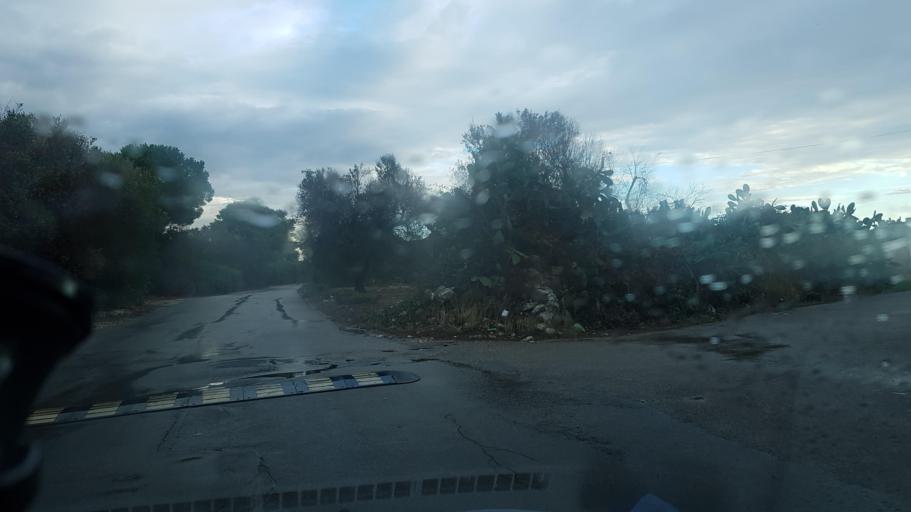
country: IT
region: Apulia
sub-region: Provincia di Lecce
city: Giorgilorio
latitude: 40.3833
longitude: 18.1458
